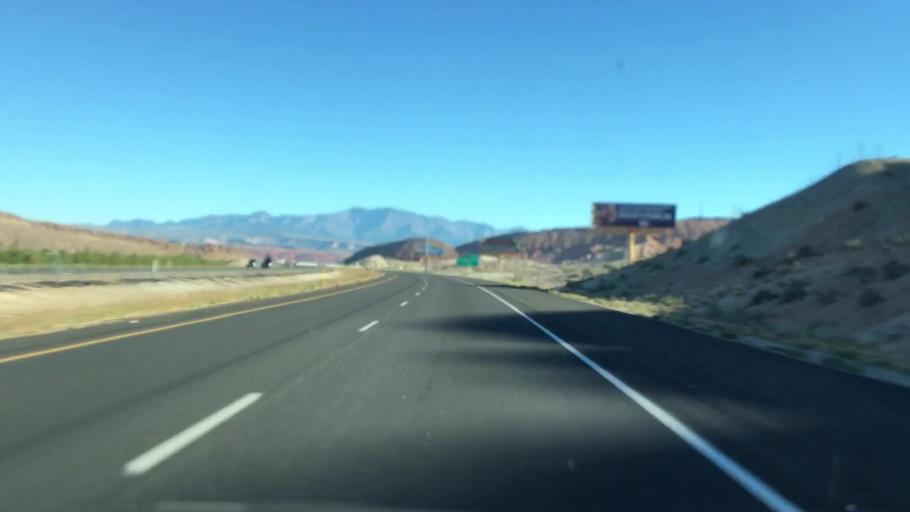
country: US
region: Utah
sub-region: Washington County
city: Saint George
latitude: 37.0477
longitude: -113.5893
